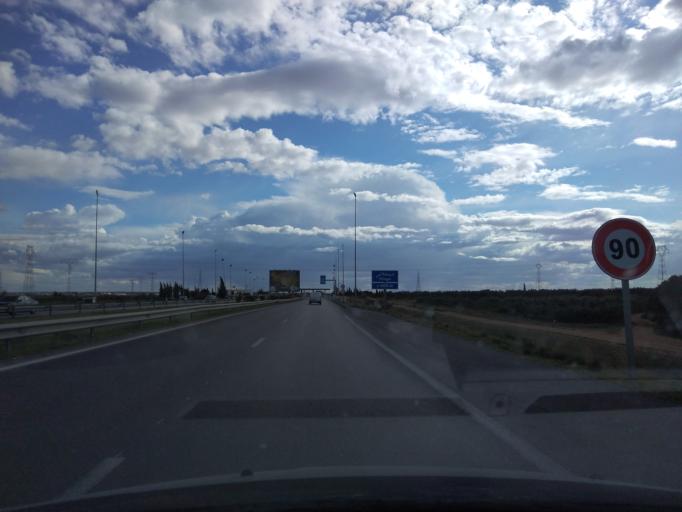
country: TN
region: Susah
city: Masakin
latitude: 35.6944
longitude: 10.5643
